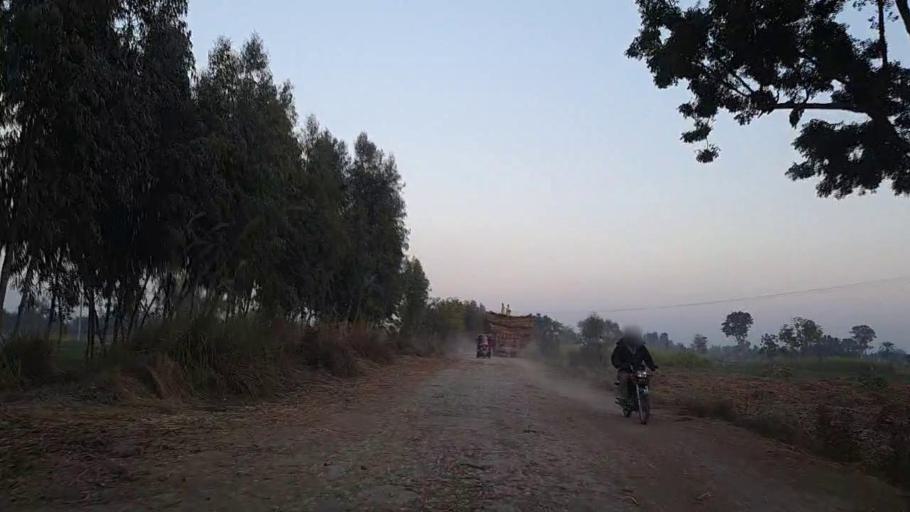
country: PK
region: Sindh
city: Naushahro Firoz
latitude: 26.7999
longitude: 68.0283
